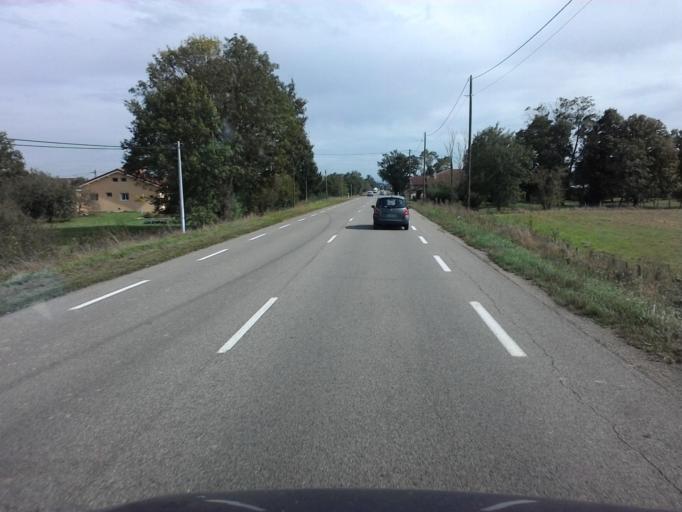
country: FR
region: Rhone-Alpes
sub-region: Departement de l'Ain
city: Polliat
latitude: 46.2516
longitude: 5.1032
